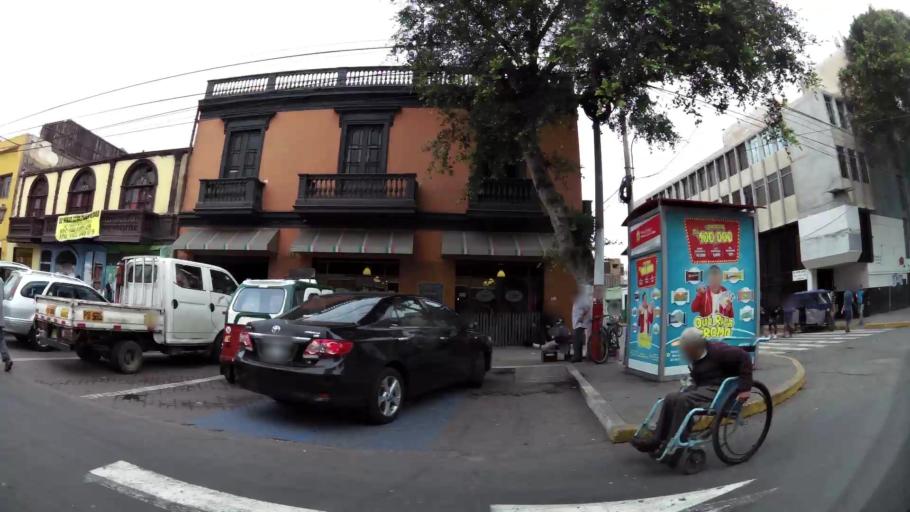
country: PE
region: Callao
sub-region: Callao
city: Callao
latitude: -12.0612
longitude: -77.1444
